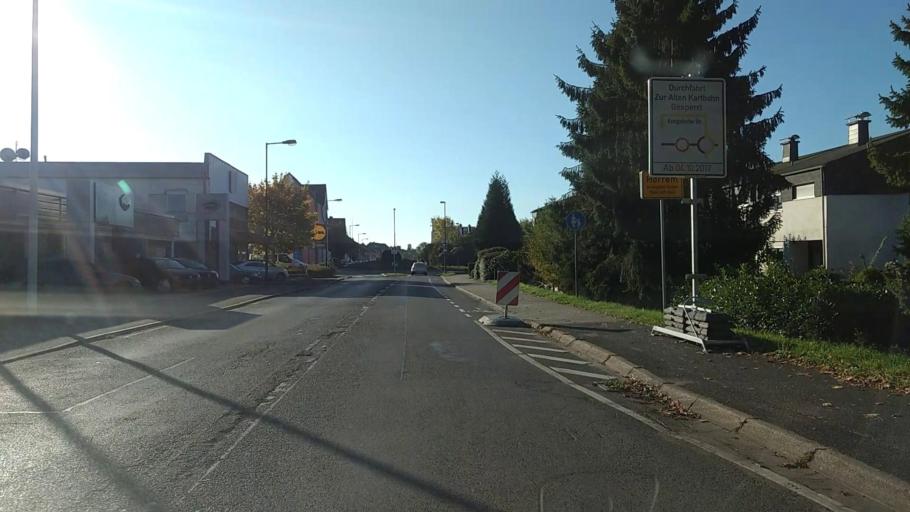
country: DE
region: North Rhine-Westphalia
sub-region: Regierungsbezirk Koln
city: Kerpen
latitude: 50.9235
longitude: 6.7062
